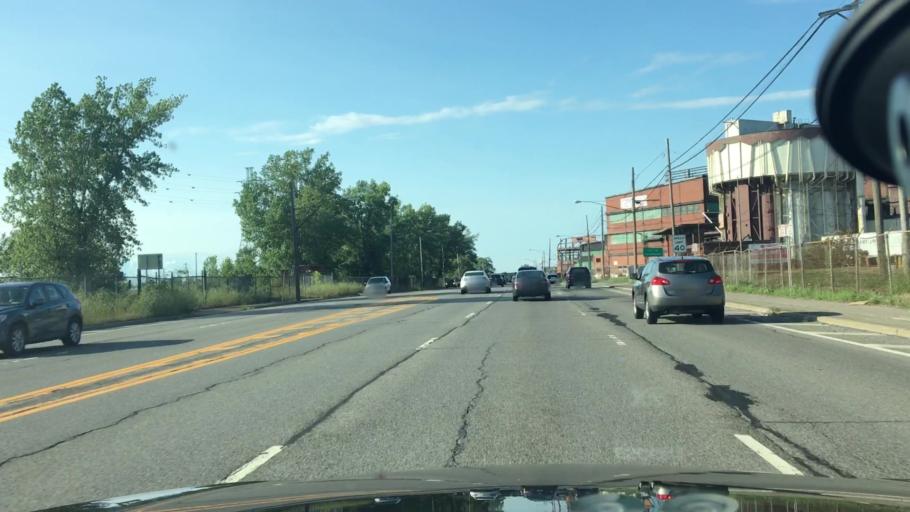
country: US
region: New York
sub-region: Erie County
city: Blasdell
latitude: 42.8048
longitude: -78.8461
